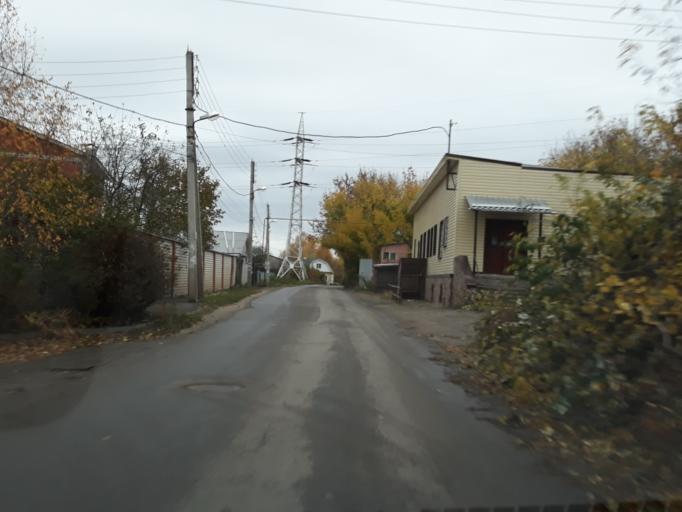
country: RU
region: Nizjnij Novgorod
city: Nizhniy Novgorod
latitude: 56.2520
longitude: 43.9818
